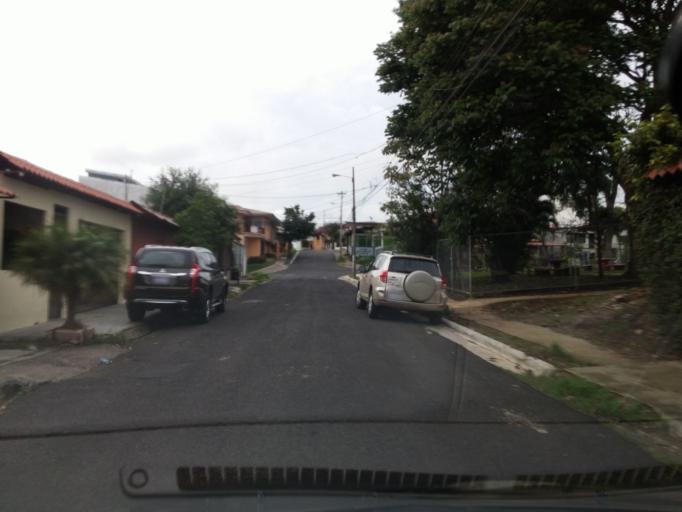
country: CR
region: Heredia
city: Heredia
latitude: 10.0158
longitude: -84.1205
